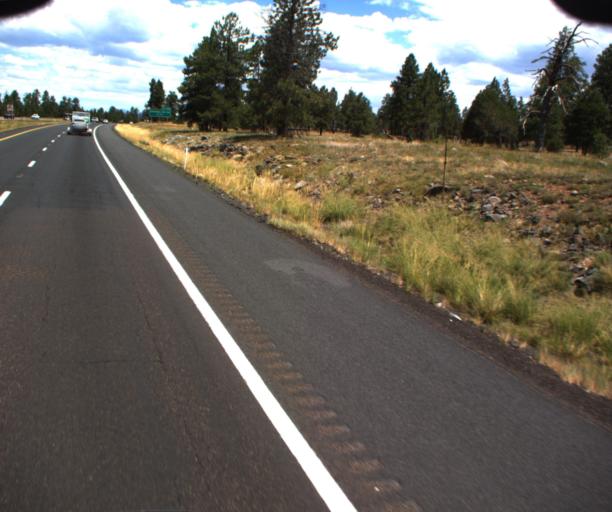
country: US
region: Arizona
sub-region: Coconino County
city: Sedona
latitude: 34.9008
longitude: -111.6416
